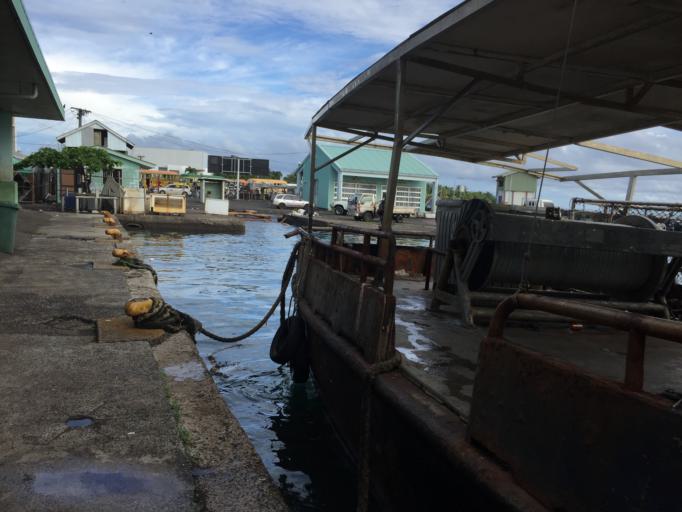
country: WS
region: Tuamasaga
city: Apia
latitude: -13.8294
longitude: -171.7701
